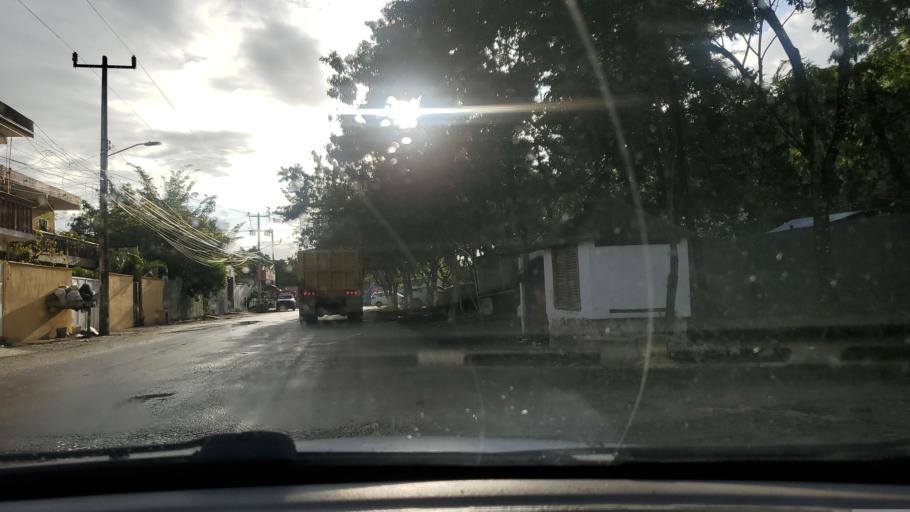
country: MX
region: Quintana Roo
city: Tulum
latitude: 20.2098
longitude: -87.4715
